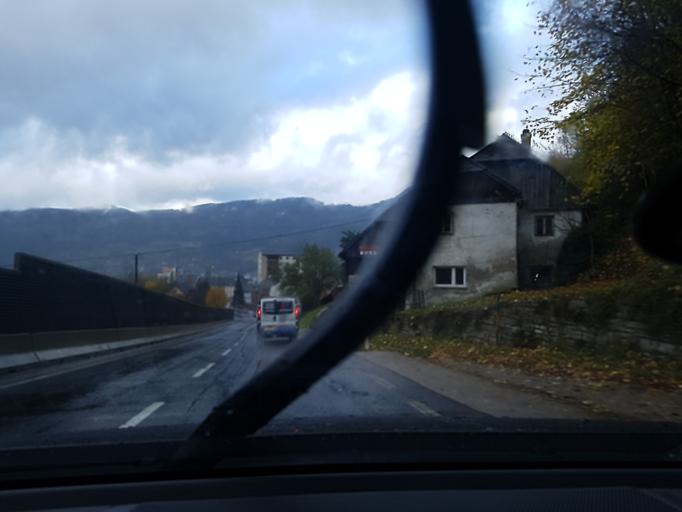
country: AT
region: Styria
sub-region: Politischer Bezirk Liezen
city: Trieben
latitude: 47.4820
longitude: 14.4875
